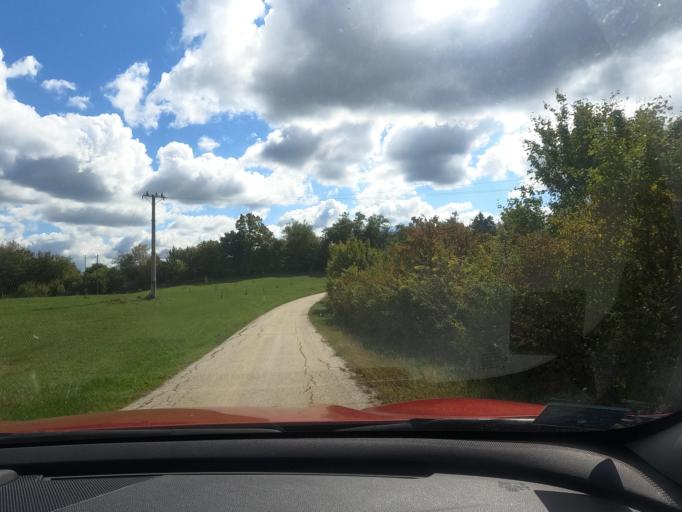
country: HR
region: Karlovacka
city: Vojnic
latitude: 45.2351
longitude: 15.7079
